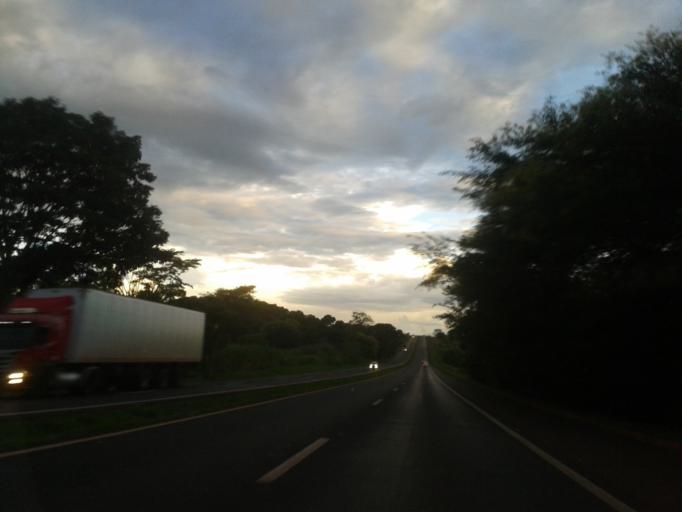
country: BR
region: Minas Gerais
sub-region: Centralina
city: Centralina
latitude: -18.6584
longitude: -49.1683
